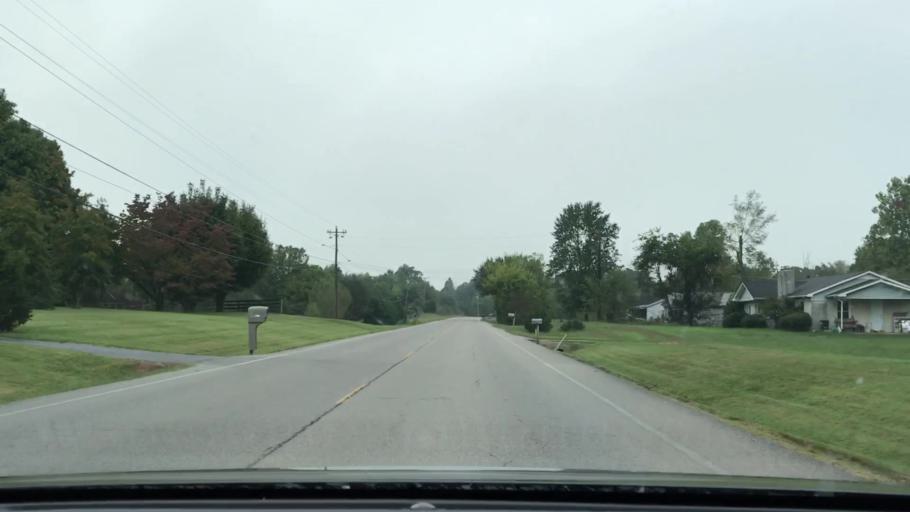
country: US
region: Tennessee
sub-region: Sumner County
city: Portland
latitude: 36.4955
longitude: -86.4962
